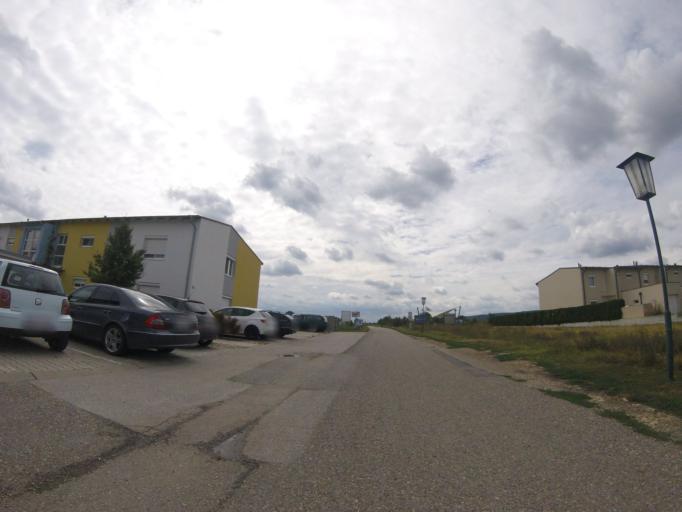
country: AT
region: Burgenland
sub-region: Politischer Bezirk Neusiedl am See
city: Winden am See
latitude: 47.9463
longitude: 16.7543
